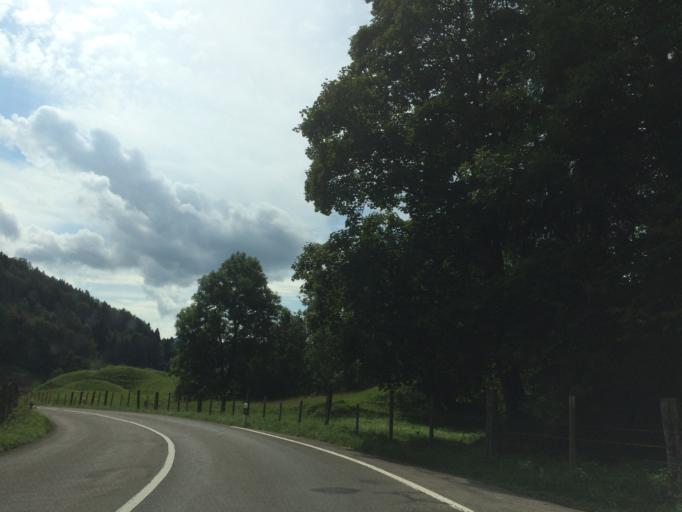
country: CH
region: Saint Gallen
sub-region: Wahlkreis Toggenburg
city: Krummenau
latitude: 47.2433
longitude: 9.2276
